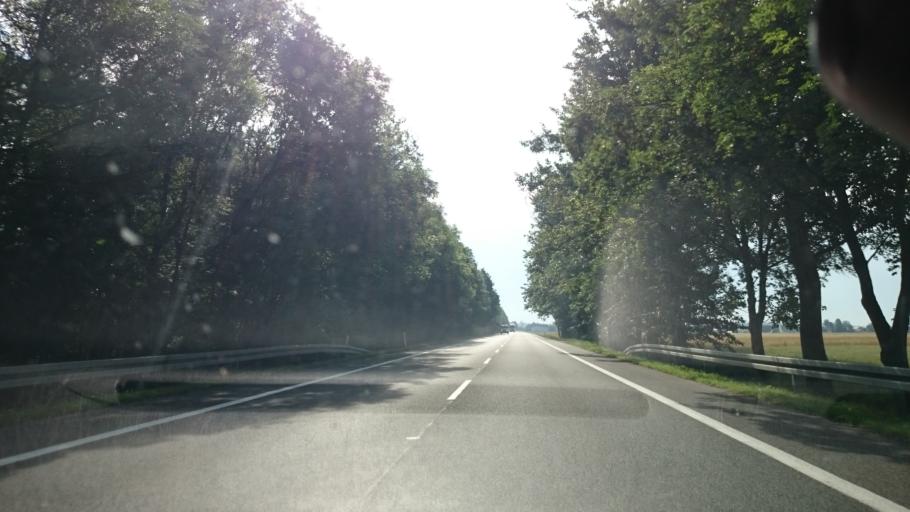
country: PL
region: Opole Voivodeship
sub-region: Powiat strzelecki
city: Jemielnica
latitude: 50.4973
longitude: 18.3629
